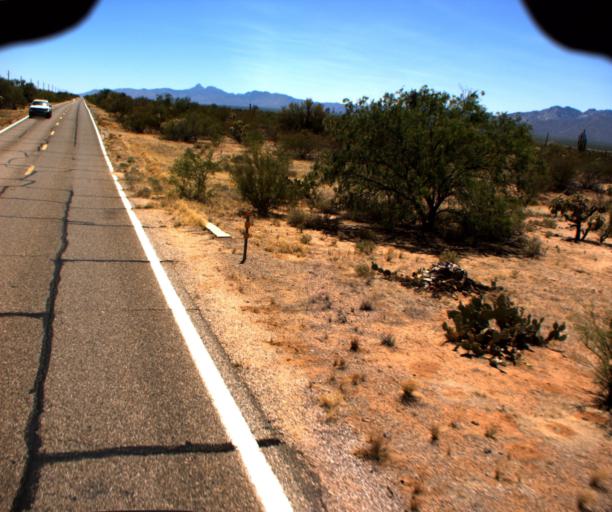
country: US
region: Arizona
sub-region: Pima County
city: Three Points
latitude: 32.0281
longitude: -111.3434
